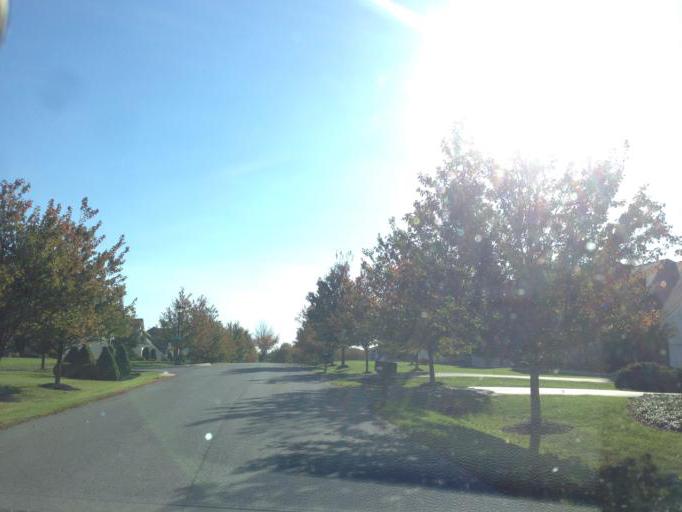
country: US
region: Maryland
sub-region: Carroll County
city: Sykesville
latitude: 39.3277
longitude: -77.0101
